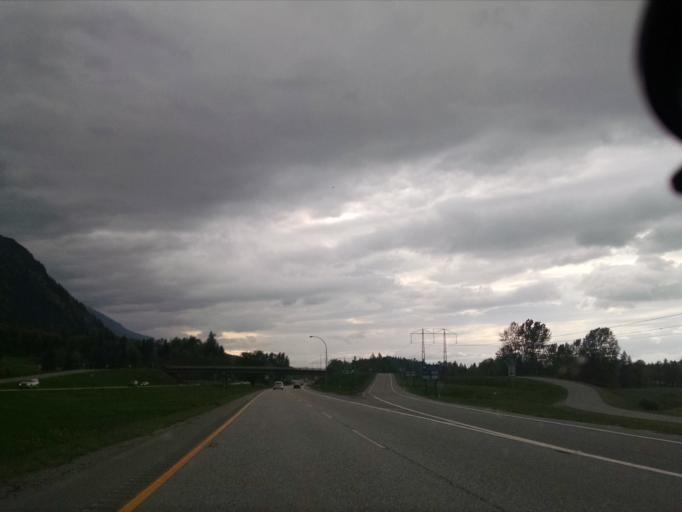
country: CA
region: British Columbia
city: Agassiz
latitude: 49.2003
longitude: -121.7259
